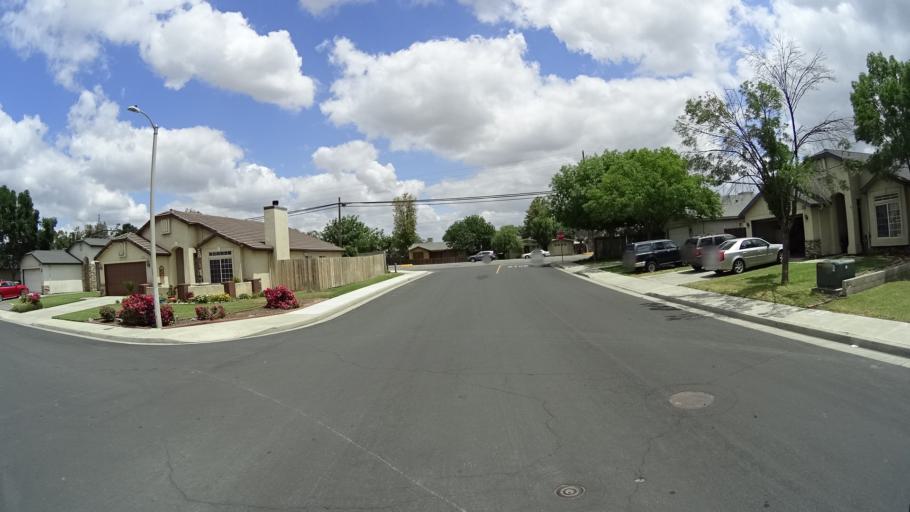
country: US
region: California
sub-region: Kings County
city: Home Garden
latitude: 36.3084
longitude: -119.6557
